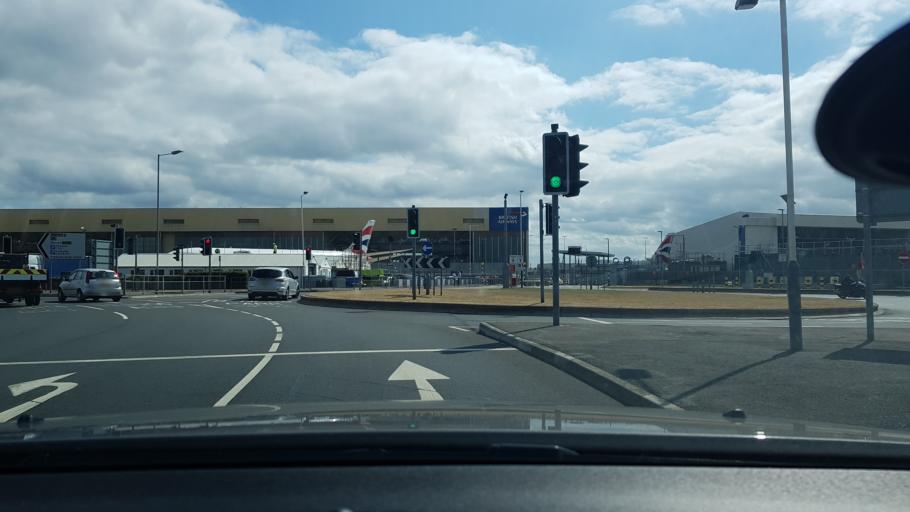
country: GB
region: England
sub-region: Greater London
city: Feltham
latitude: 51.4768
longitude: -0.4266
